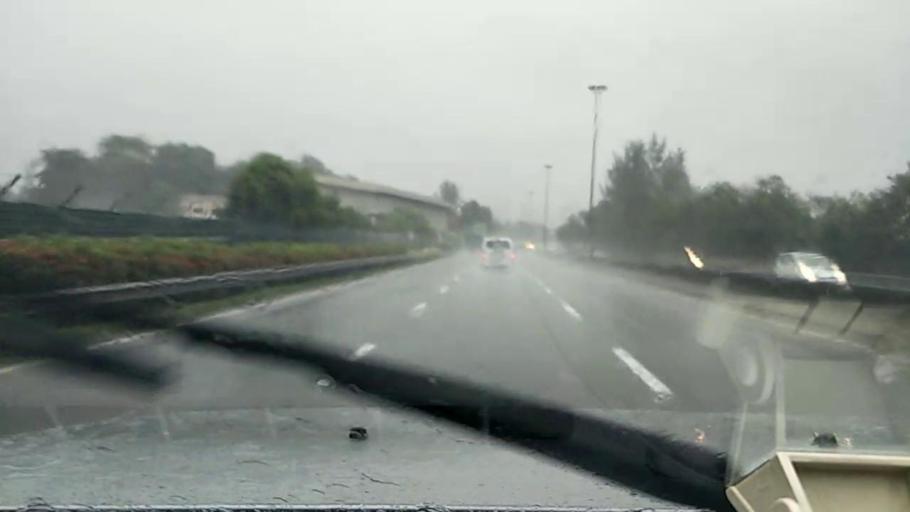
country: MY
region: Selangor
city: Kampong Baharu Balakong
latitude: 3.0023
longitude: 101.7735
